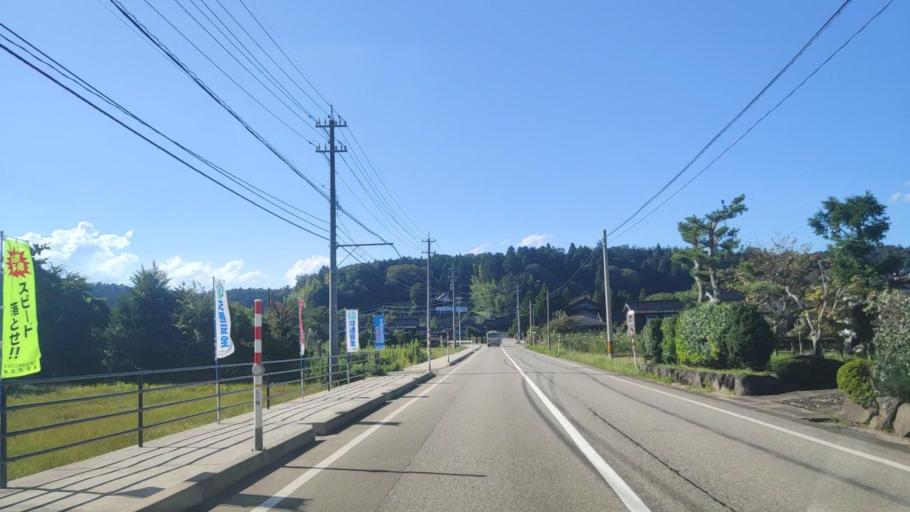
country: JP
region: Ishikawa
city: Nanao
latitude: 37.2357
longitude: 136.9646
